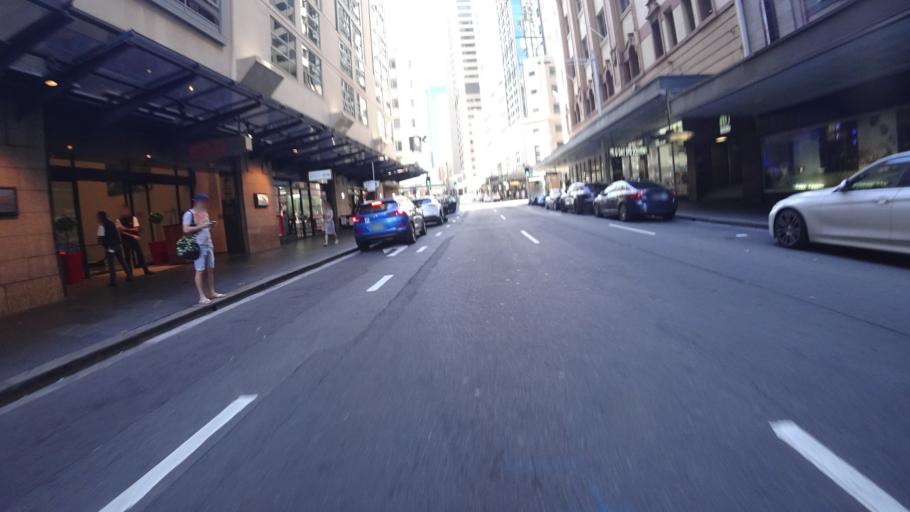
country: AU
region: New South Wales
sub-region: City of Sydney
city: Haymarket
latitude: -33.8771
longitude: 151.2079
